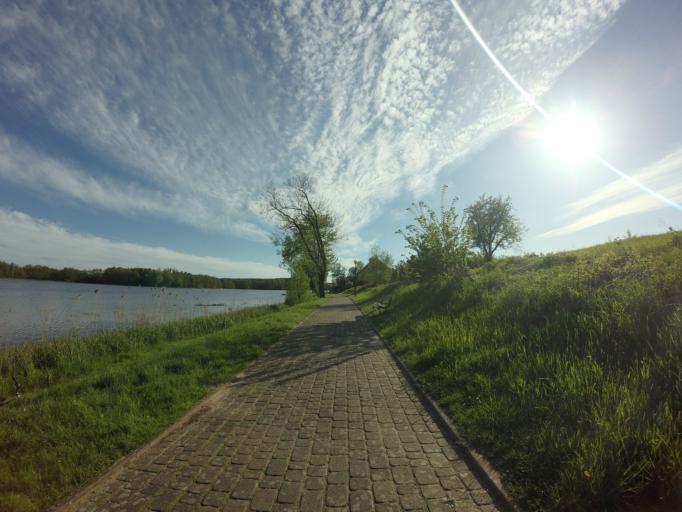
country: PL
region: West Pomeranian Voivodeship
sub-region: Powiat choszczenski
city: Drawno
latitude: 53.2153
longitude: 15.7537
